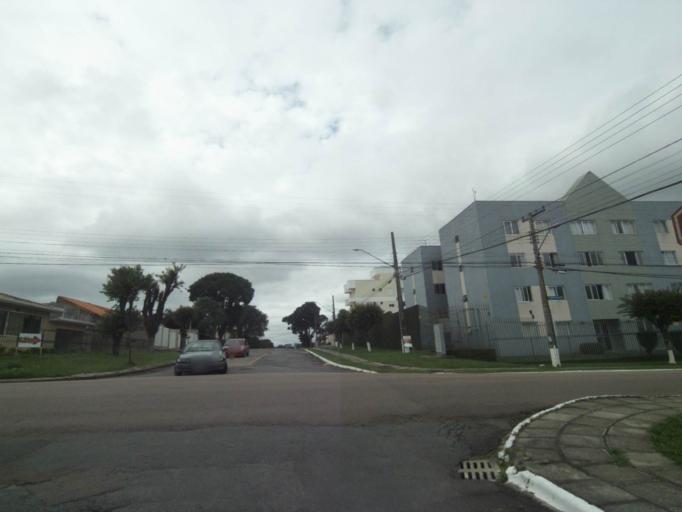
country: BR
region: Parana
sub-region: Curitiba
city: Curitiba
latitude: -25.4833
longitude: -49.2819
